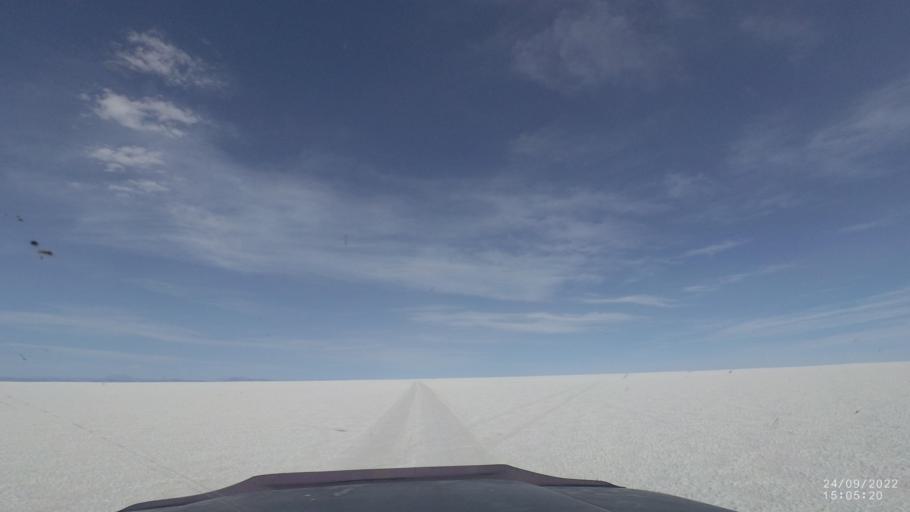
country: BO
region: Potosi
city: Colchani
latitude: -19.9054
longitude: -67.5184
